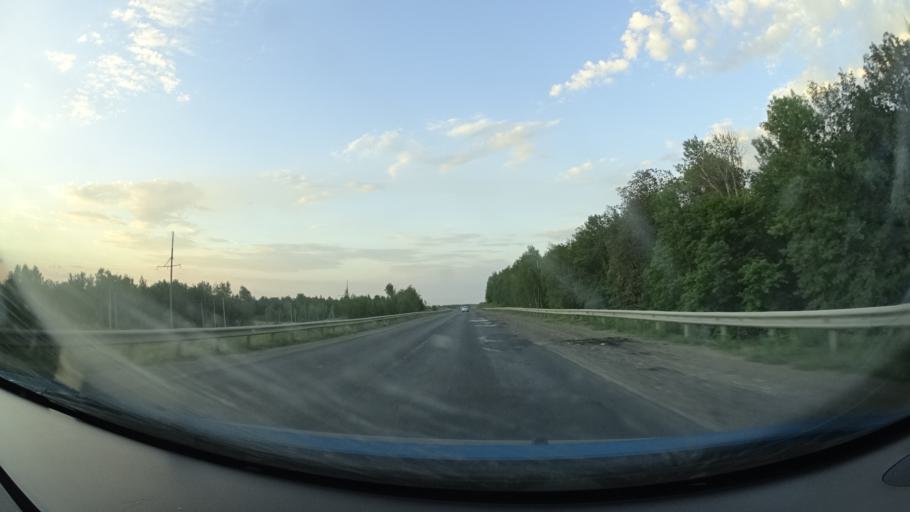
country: RU
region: Orenburg
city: Severnoye
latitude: 54.1774
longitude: 52.6542
